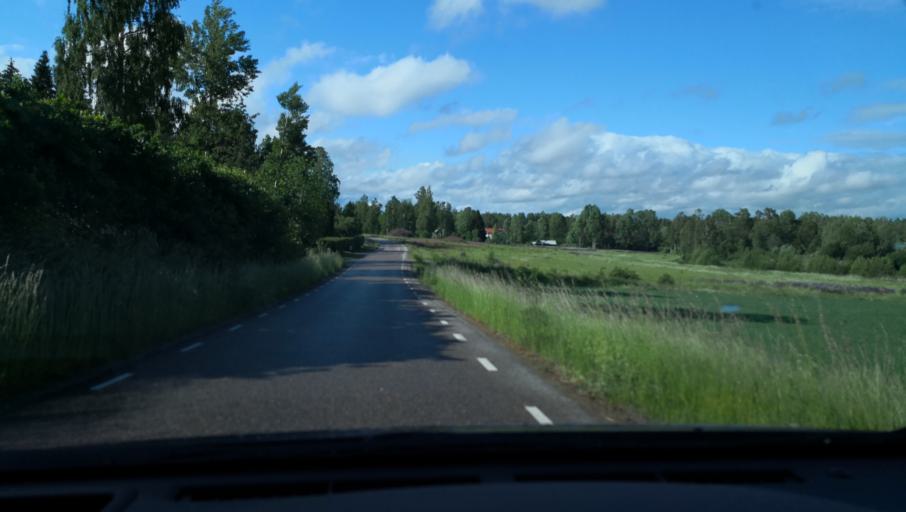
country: SE
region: OErebro
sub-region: Lindesbergs Kommun
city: Fellingsbro
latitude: 59.3229
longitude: 15.6780
